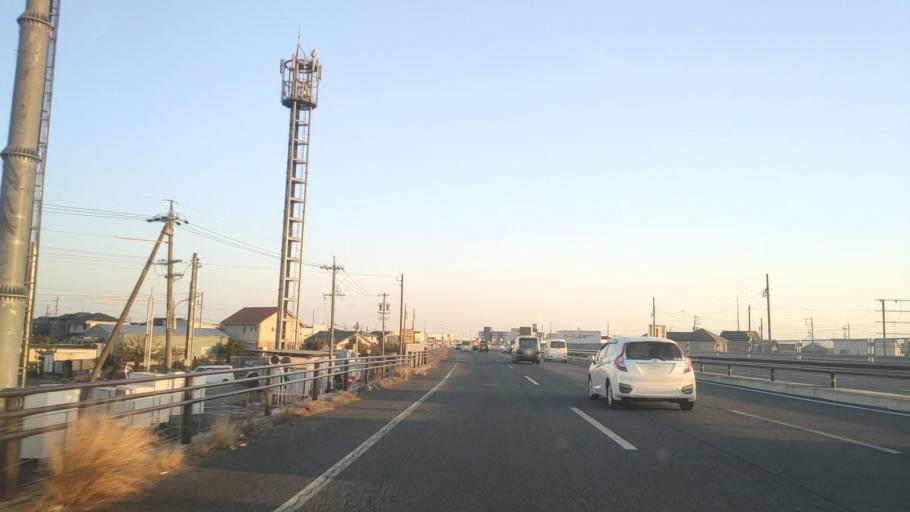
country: JP
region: Aichi
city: Kuroda
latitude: 35.3592
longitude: 136.7840
